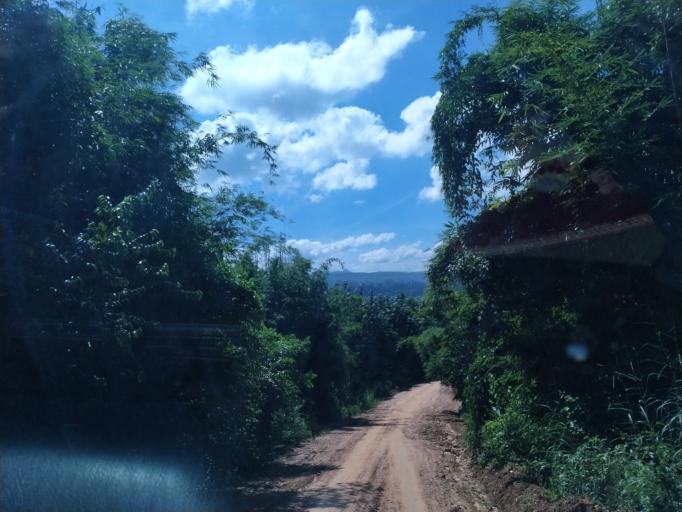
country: LA
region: Vientiane
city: Muang Phon-Hong
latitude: 18.6235
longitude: 102.8748
